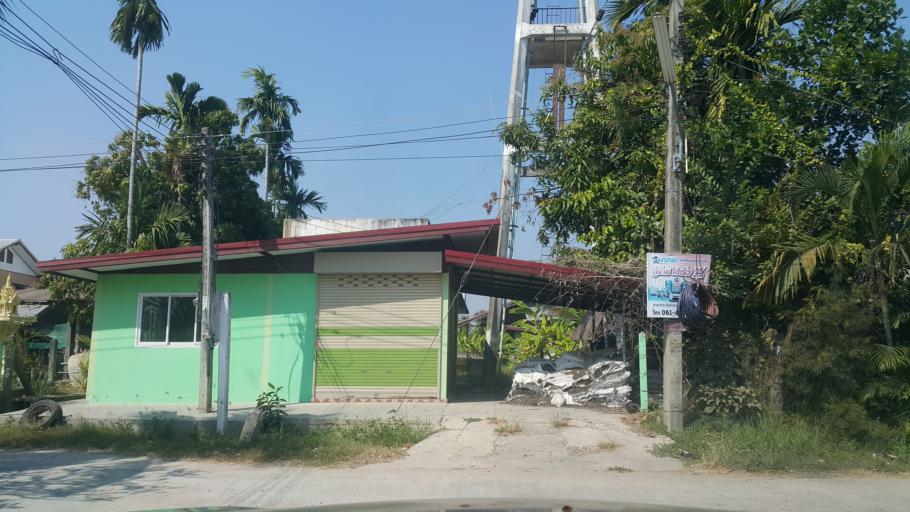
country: TH
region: Buriram
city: Krasang
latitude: 15.0533
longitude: 103.3843
